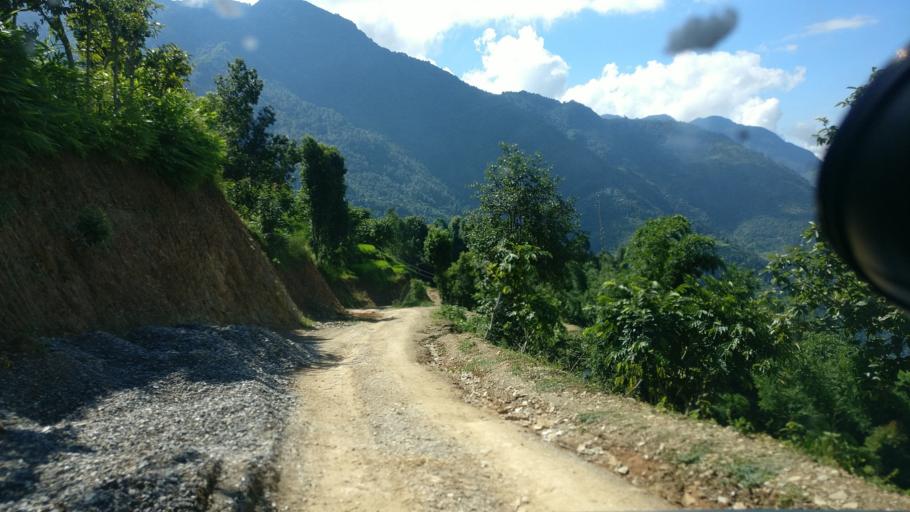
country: NP
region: Western Region
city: Baglung
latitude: 28.1402
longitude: 83.6491
